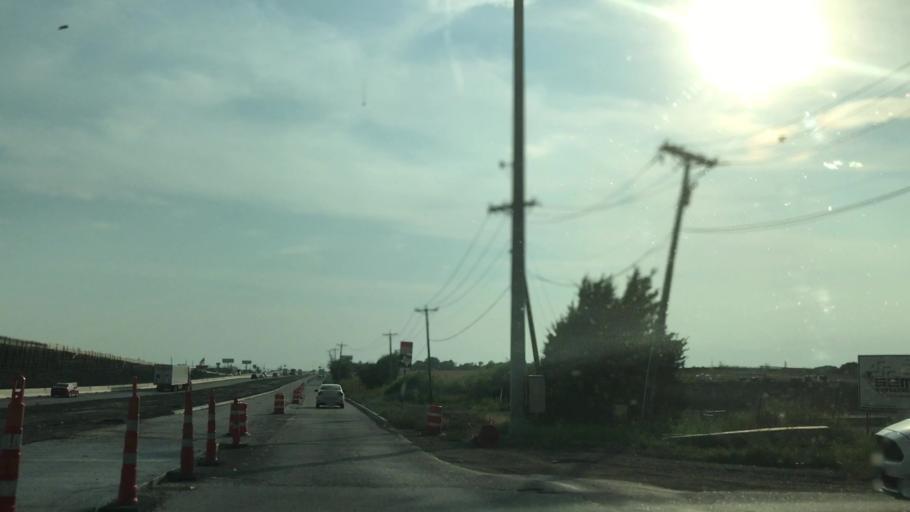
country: US
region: Texas
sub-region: Rockwall County
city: Rockwall
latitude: 32.9200
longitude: -96.4187
